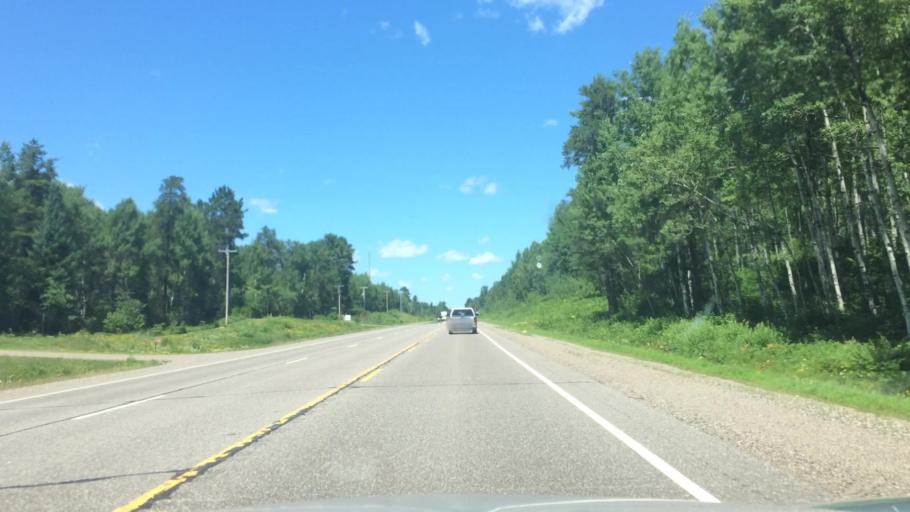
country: US
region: Wisconsin
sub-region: Lincoln County
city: Tomahawk
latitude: 45.6749
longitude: -89.7141
